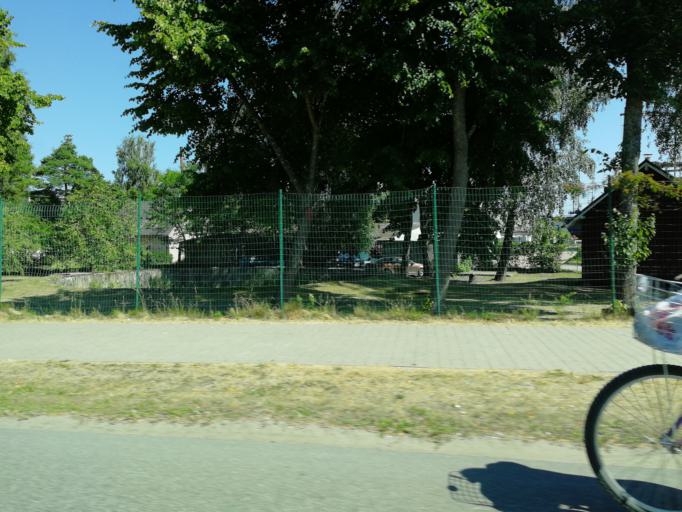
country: LV
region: Rojas
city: Roja
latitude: 57.5071
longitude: 22.8004
